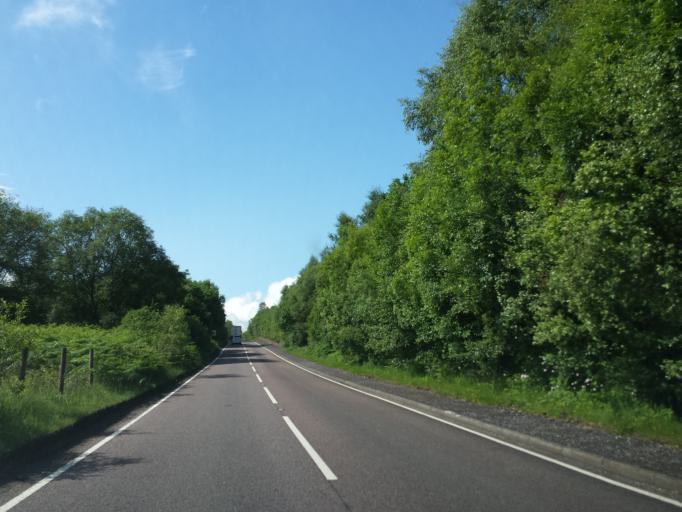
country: GB
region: Scotland
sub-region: Argyll and Bute
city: Garelochhead
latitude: 56.4080
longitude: -5.0321
